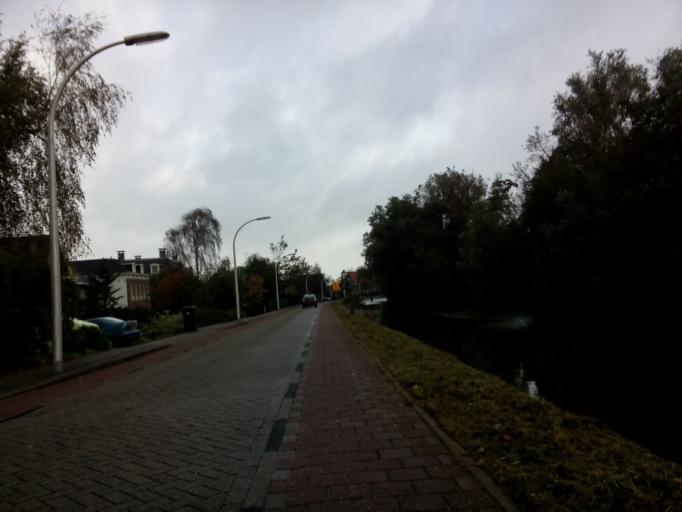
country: NL
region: South Holland
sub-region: Gemeente Maassluis
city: Maassluis
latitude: 51.9308
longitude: 4.2697
